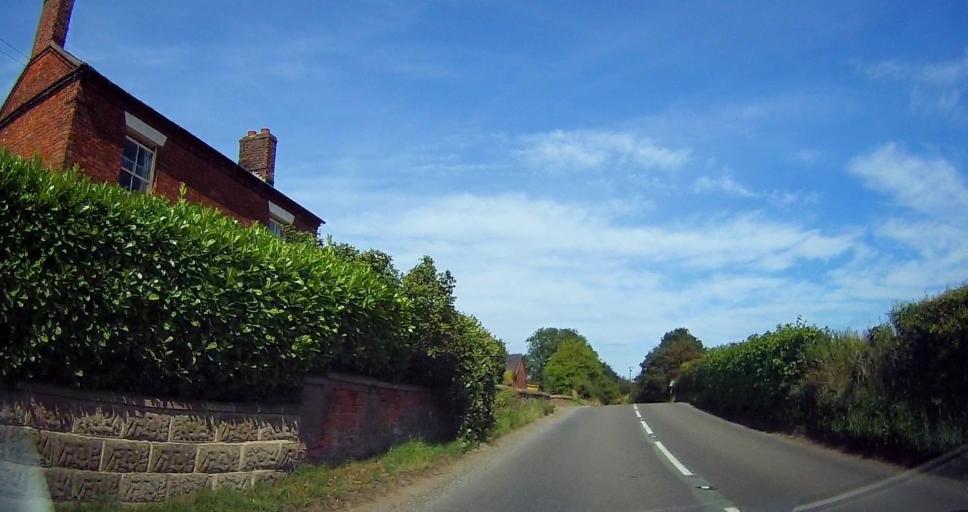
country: GB
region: England
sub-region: Shropshire
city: Market Drayton
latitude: 52.9742
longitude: -2.5183
